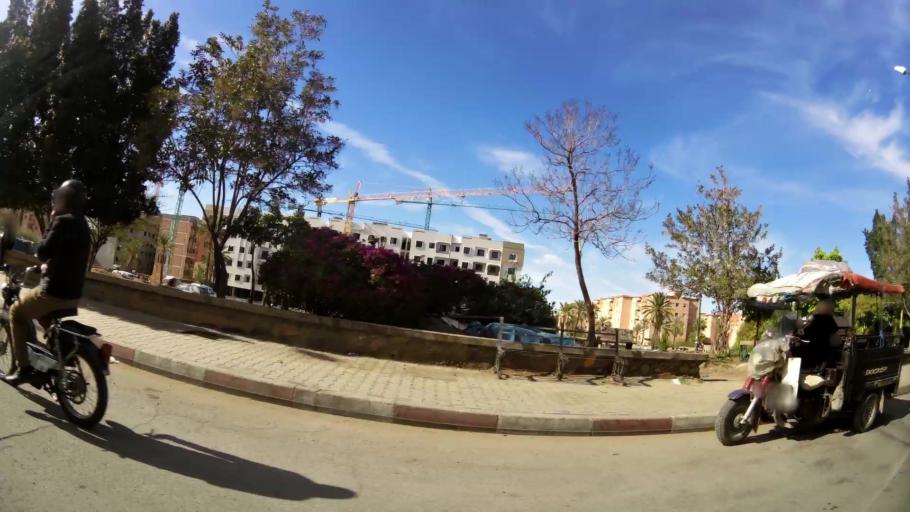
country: MA
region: Marrakech-Tensift-Al Haouz
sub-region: Marrakech
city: Marrakesh
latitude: 31.6532
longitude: -8.0278
